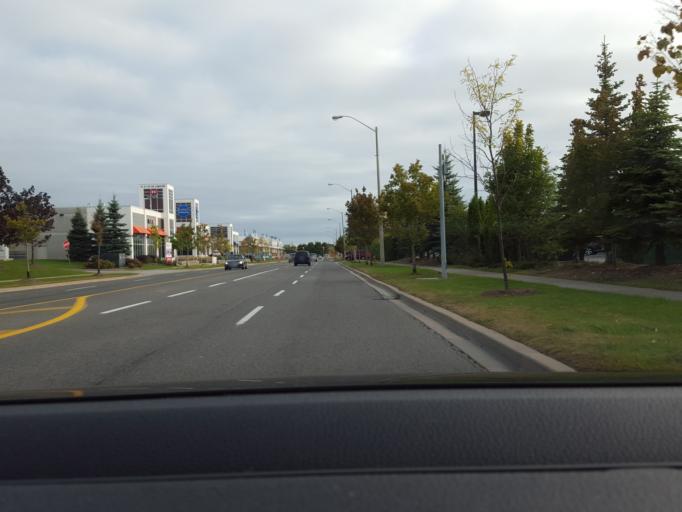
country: CA
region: Ontario
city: Scarborough
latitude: 43.7239
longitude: -79.2902
